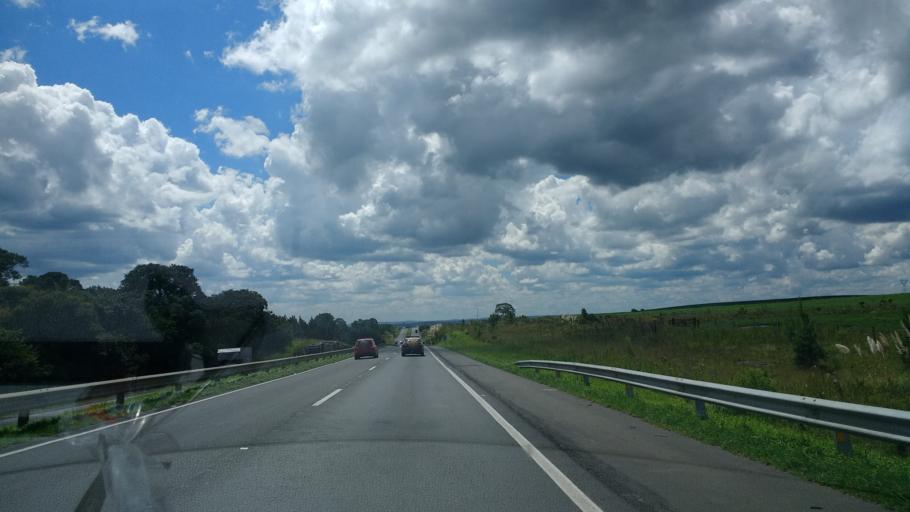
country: BR
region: Parana
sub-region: Palmeira
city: Palmeira
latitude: -25.3910
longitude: -49.7982
